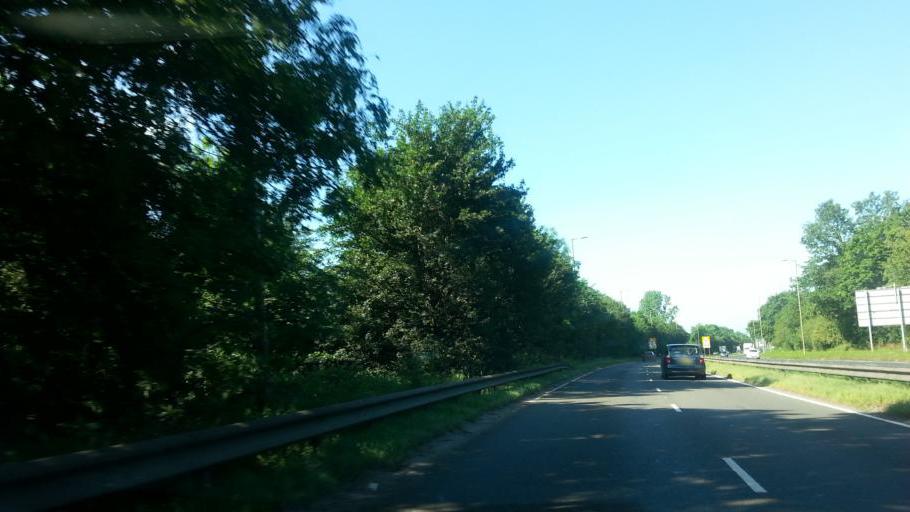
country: GB
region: England
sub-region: Hertfordshire
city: Hatfield
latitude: 51.7500
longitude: -0.2501
